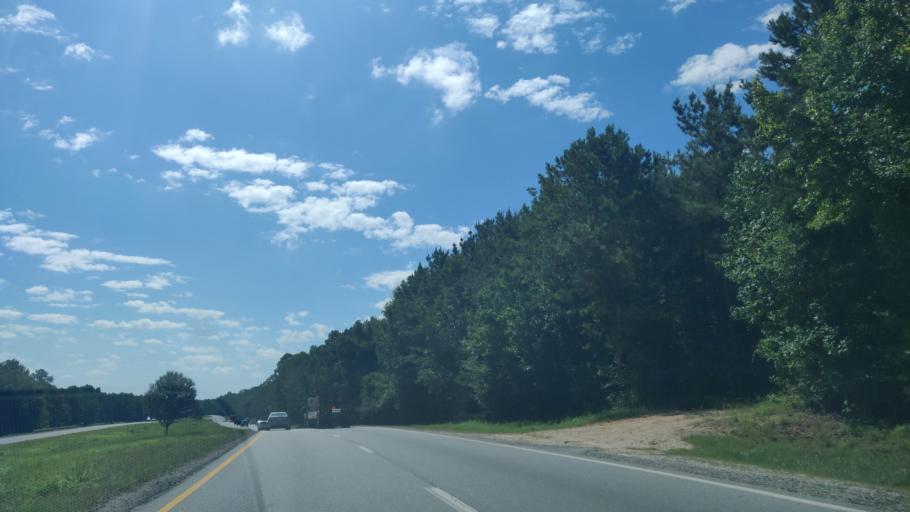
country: US
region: Alabama
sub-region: Lee County
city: Opelika
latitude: 32.6383
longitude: -85.3106
